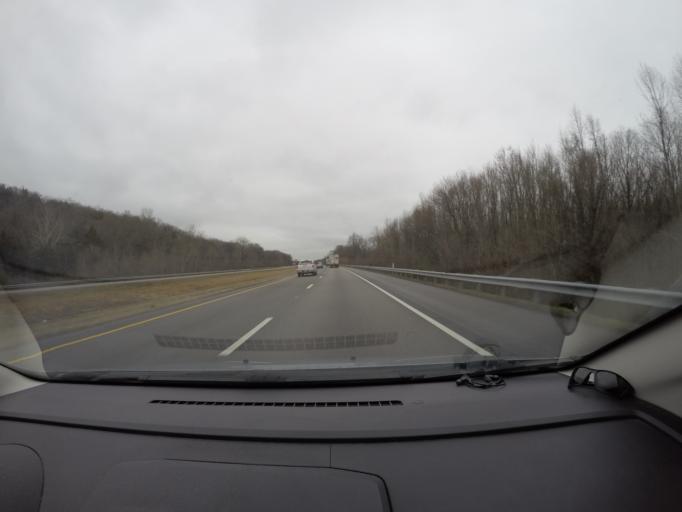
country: US
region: Tennessee
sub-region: Marion County
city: South Pittsburg
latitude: 35.0588
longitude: -85.7220
